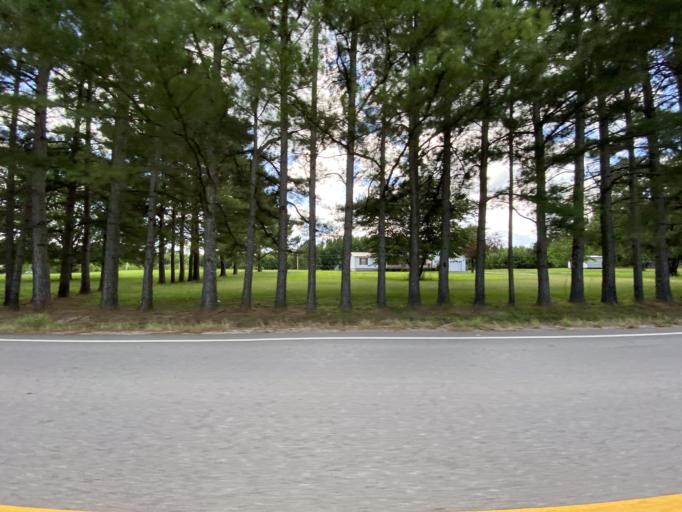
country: US
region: Alabama
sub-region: Lauderdale County
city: Underwood-Petersville
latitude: 34.9374
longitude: -87.8534
